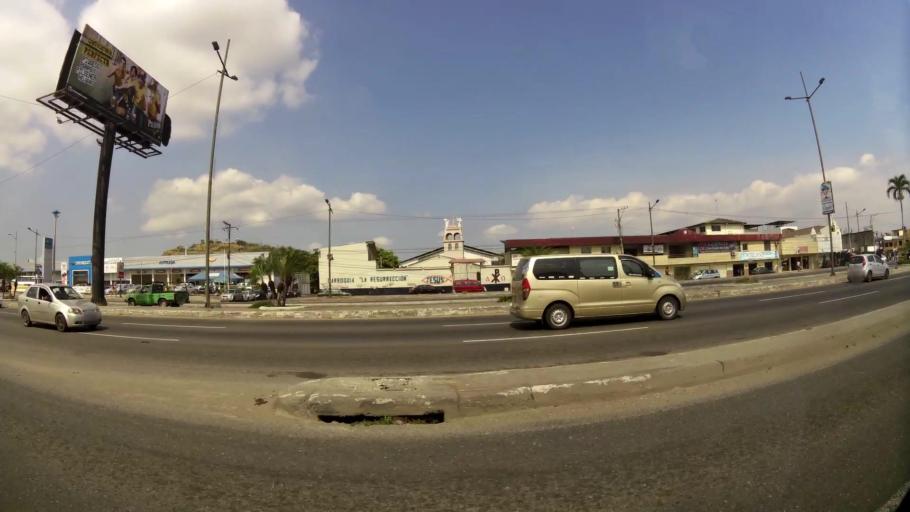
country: EC
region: Guayas
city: Eloy Alfaro
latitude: -2.1672
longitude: -79.8422
